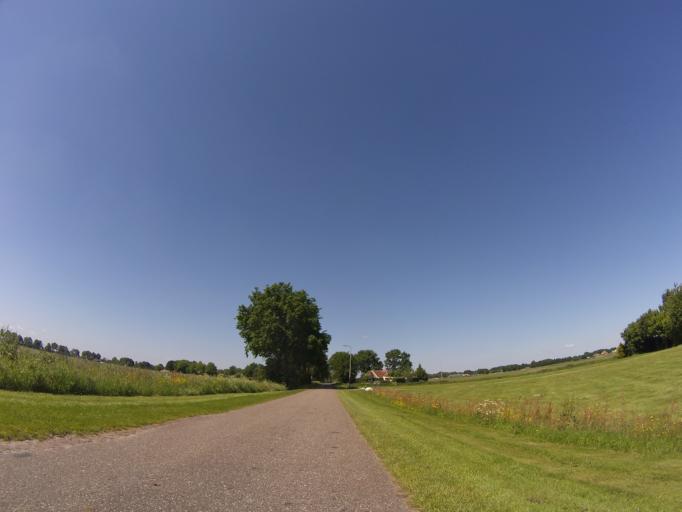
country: NL
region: Drenthe
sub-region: Gemeente Coevorden
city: Dalen
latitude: 52.7629
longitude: 6.6229
